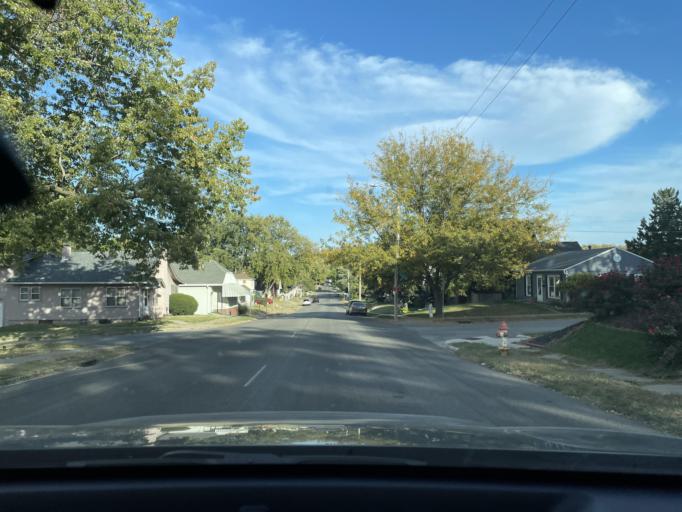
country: US
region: Missouri
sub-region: Buchanan County
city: Saint Joseph
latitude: 39.7683
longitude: -94.8270
